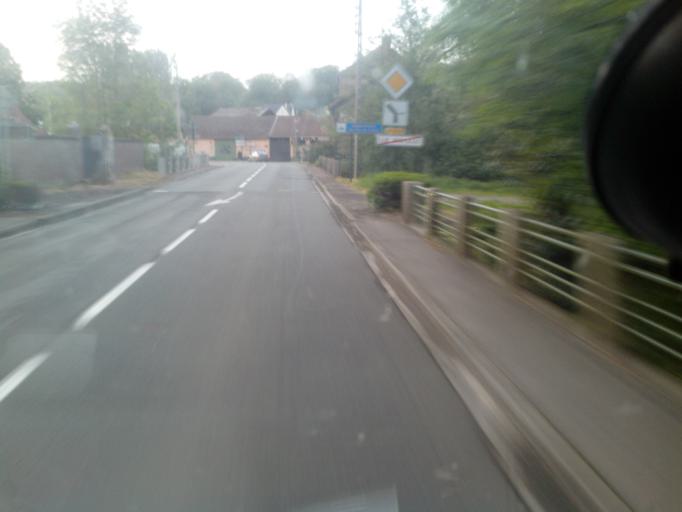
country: FR
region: Nord-Pas-de-Calais
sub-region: Departement du Pas-de-Calais
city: Marconnelle
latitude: 50.2769
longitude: 1.9883
